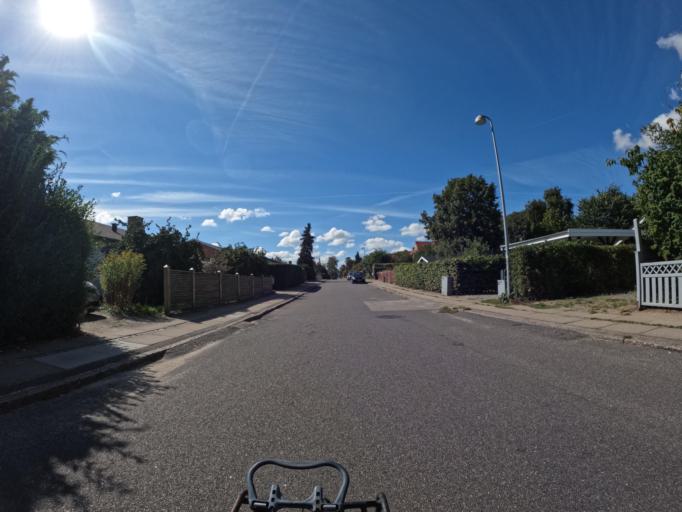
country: DK
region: Capital Region
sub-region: Hoje-Taastrup Kommune
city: Taastrup
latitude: 55.6551
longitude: 12.3167
